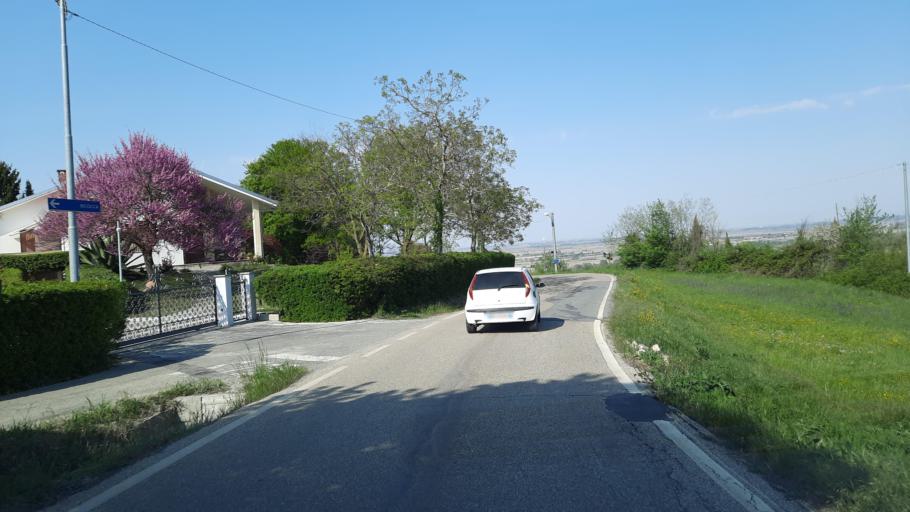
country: IT
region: Piedmont
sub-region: Provincia di Torino
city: Valentino
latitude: 45.1658
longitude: 8.1049
